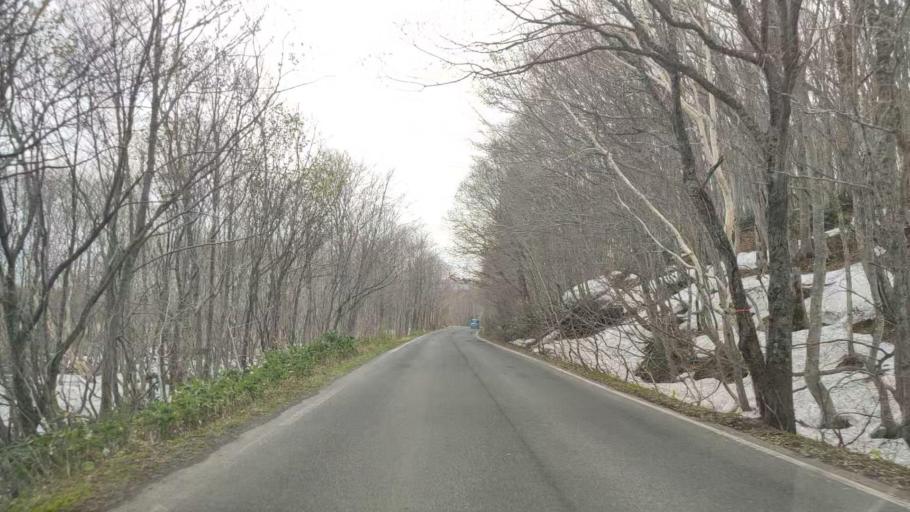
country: JP
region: Aomori
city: Aomori Shi
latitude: 40.6816
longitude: 140.9330
